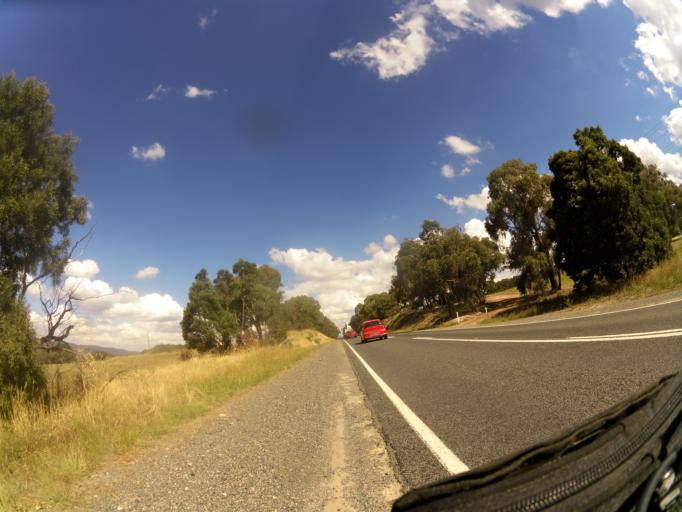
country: AU
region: Victoria
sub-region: Mansfield
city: Mansfield
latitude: -36.8858
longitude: 145.9950
